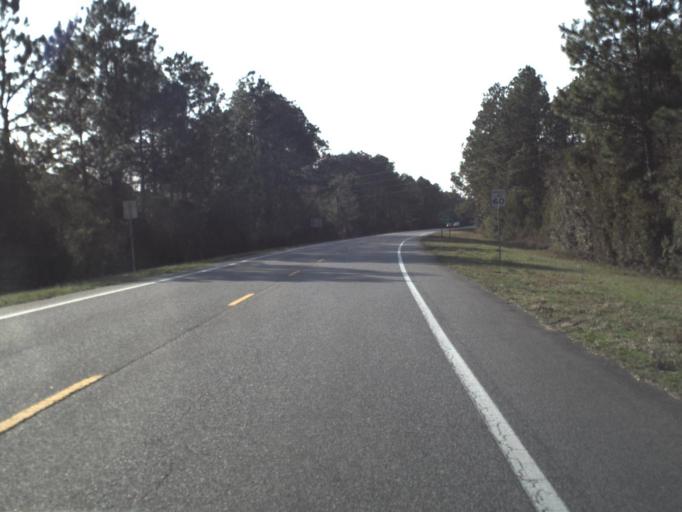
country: US
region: Florida
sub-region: Bay County
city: Laguna Beach
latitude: 30.4402
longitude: -85.8140
